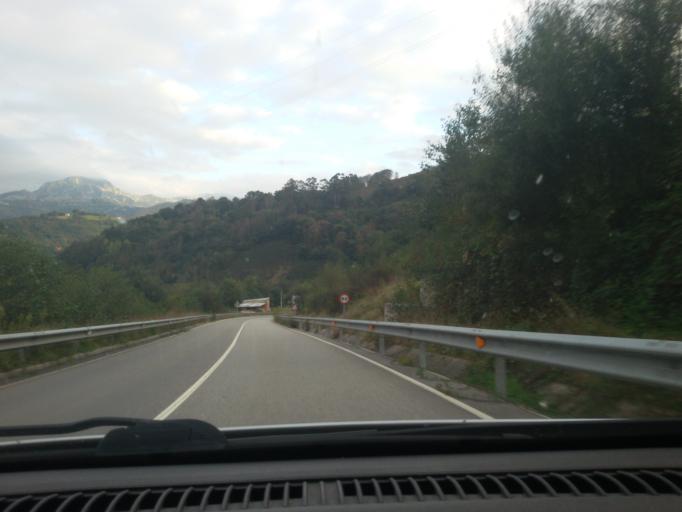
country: ES
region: Asturias
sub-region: Province of Asturias
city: Bimenes
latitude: 43.3405
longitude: -5.5792
